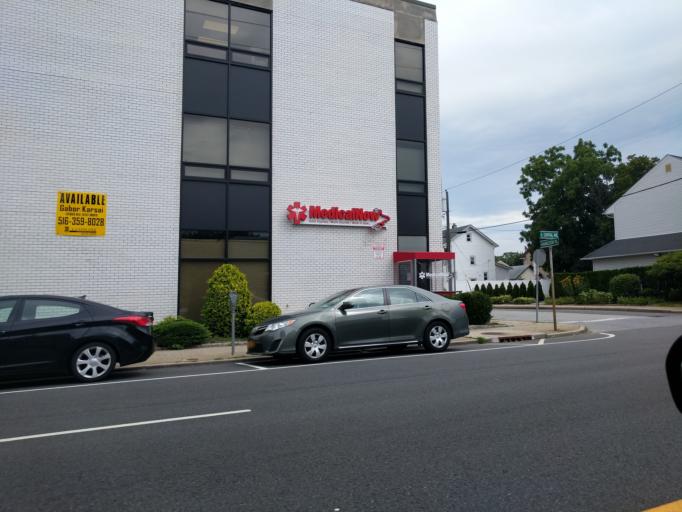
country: US
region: New York
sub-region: Nassau County
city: Valley Stream
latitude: 40.6657
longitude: -73.7085
